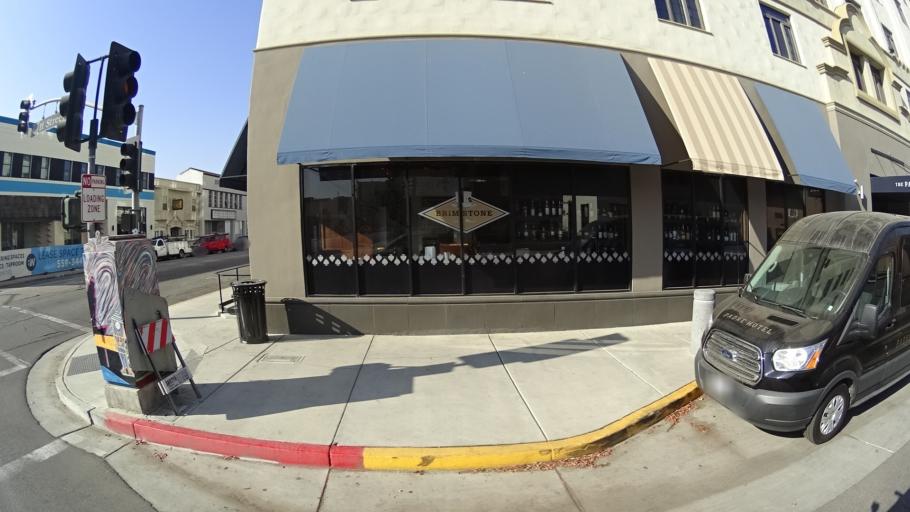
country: US
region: California
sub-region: Kern County
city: Bakersfield
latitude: 35.3755
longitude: -119.0213
